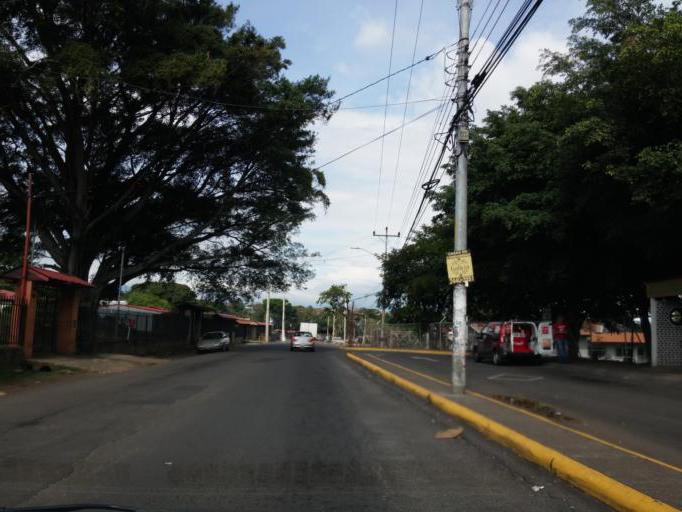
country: CR
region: Alajuela
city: Alajuela
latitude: 10.0086
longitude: -84.2104
